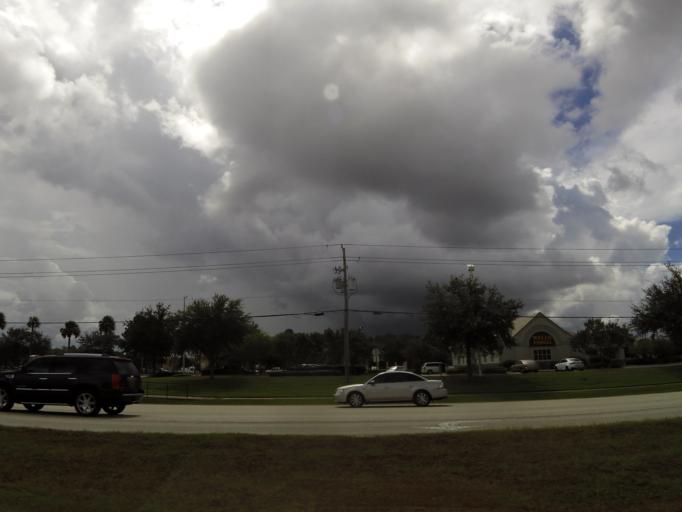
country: US
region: Florida
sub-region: Clay County
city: Orange Park
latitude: 30.1023
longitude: -81.7084
